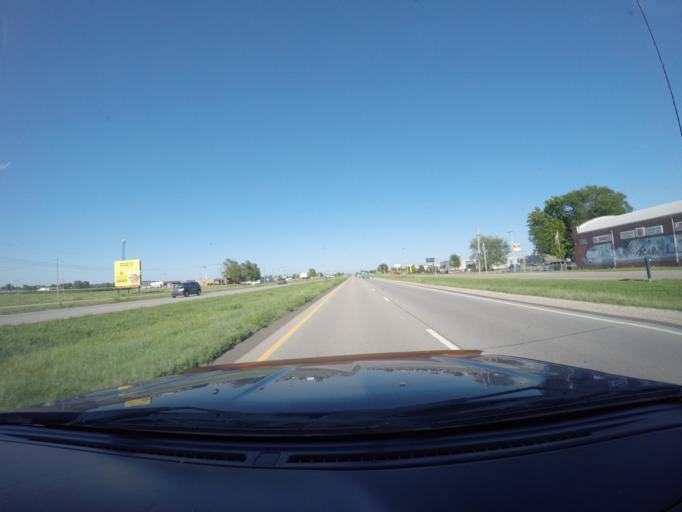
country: US
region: Kansas
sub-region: Shawnee County
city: Topeka
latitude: 39.0907
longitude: -95.7075
